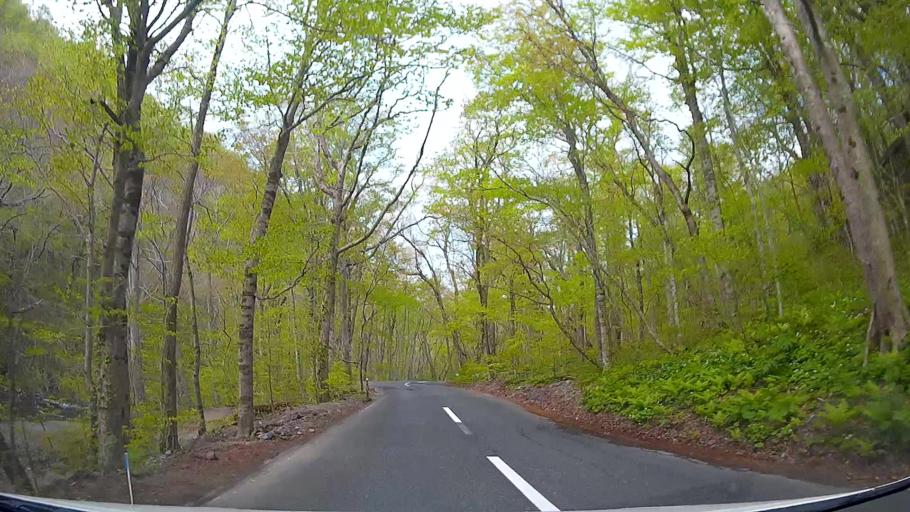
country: JP
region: Akita
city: Hanawa
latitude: 40.4827
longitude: 140.9456
